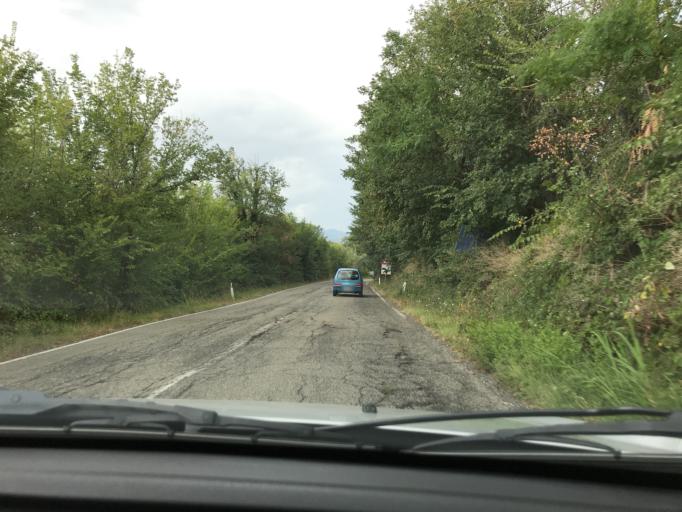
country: IT
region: Umbria
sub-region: Provincia di Terni
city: Montecchio
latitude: 42.6461
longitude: 12.2803
